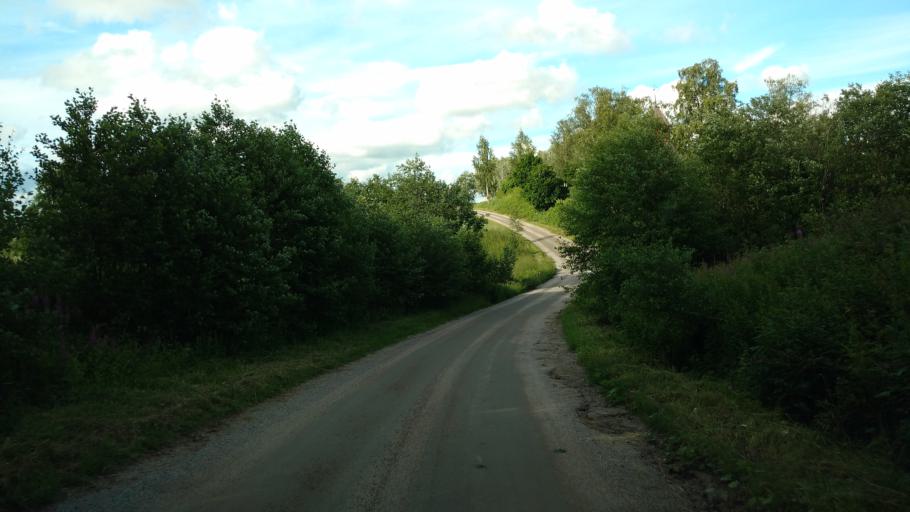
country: FI
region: Varsinais-Suomi
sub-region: Salo
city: Salo
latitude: 60.4106
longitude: 23.1666
